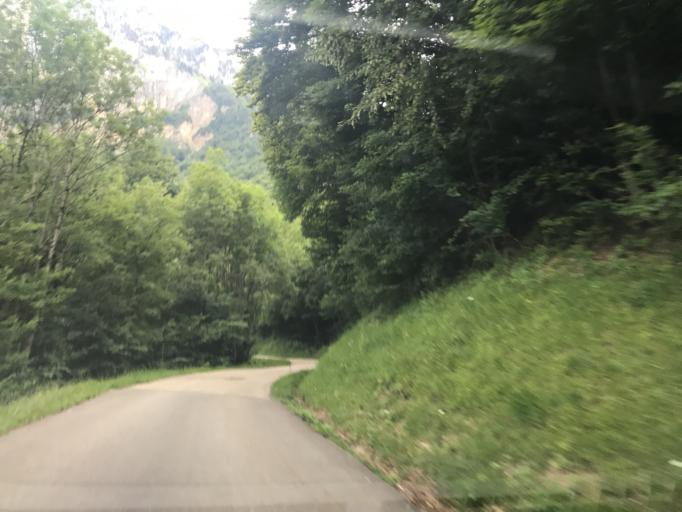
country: FR
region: Rhone-Alpes
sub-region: Departement de l'Isere
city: Saint-Vincent-de-Mercuze
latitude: 45.3791
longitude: 5.9257
